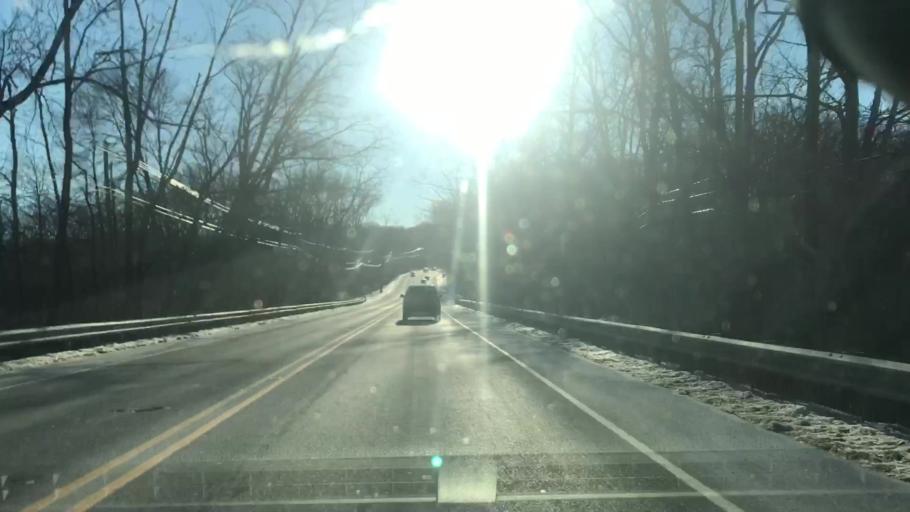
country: US
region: New Jersey
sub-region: Morris County
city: Chester
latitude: 40.7979
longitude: -74.7080
